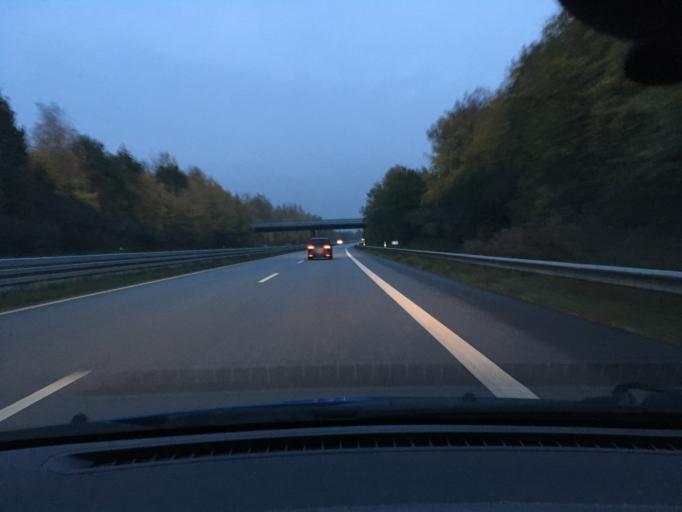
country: DE
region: Schleswig-Holstein
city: Nordhastedt
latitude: 54.1638
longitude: 9.1912
